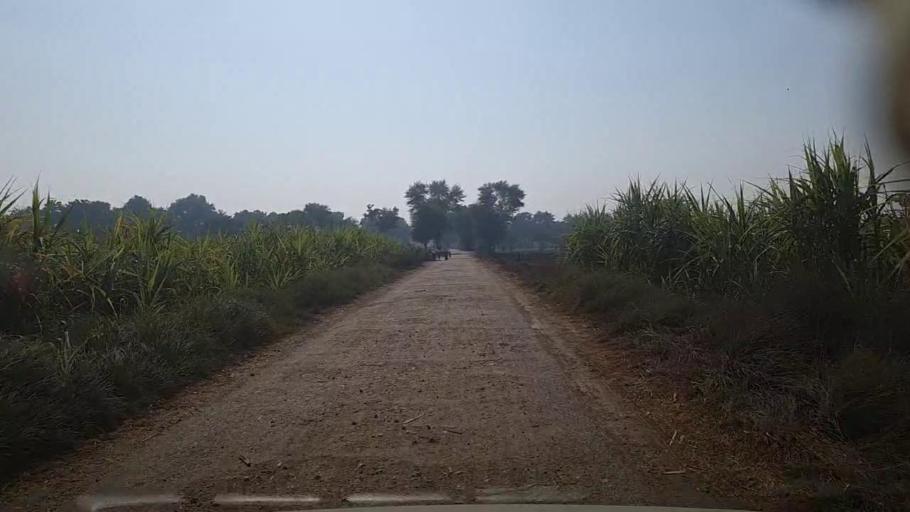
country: PK
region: Sindh
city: Kandiari
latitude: 26.9919
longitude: 68.4694
